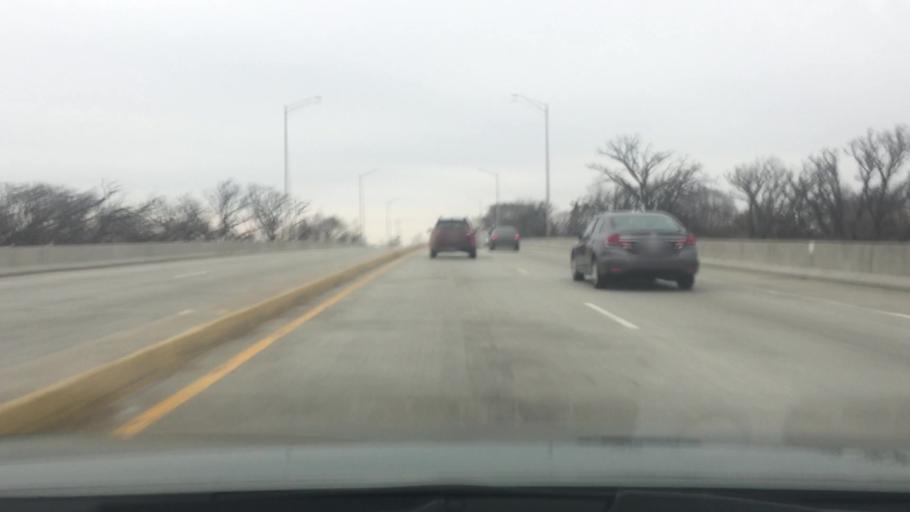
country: US
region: Illinois
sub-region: Kane County
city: Sleepy Hollow
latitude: 42.0580
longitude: -88.3373
